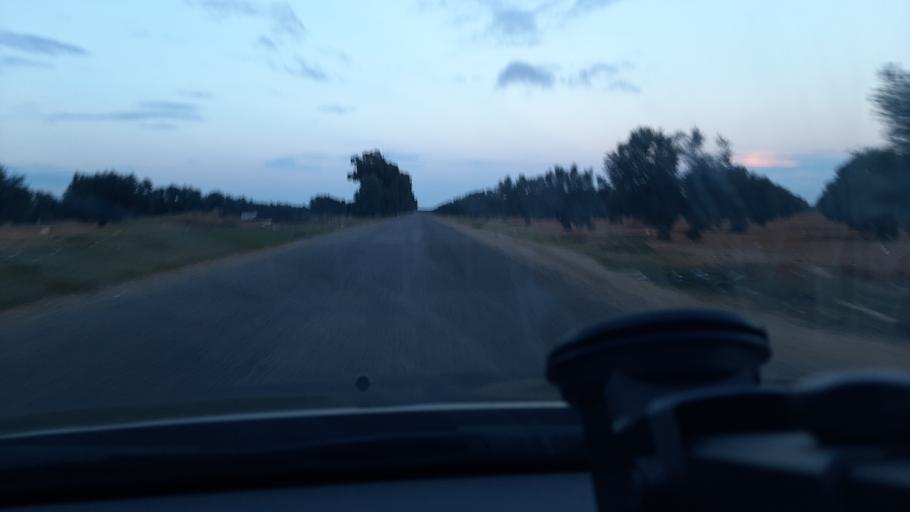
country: TN
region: Al Mahdiyah
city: Shurban
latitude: 34.9753
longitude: 10.3777
